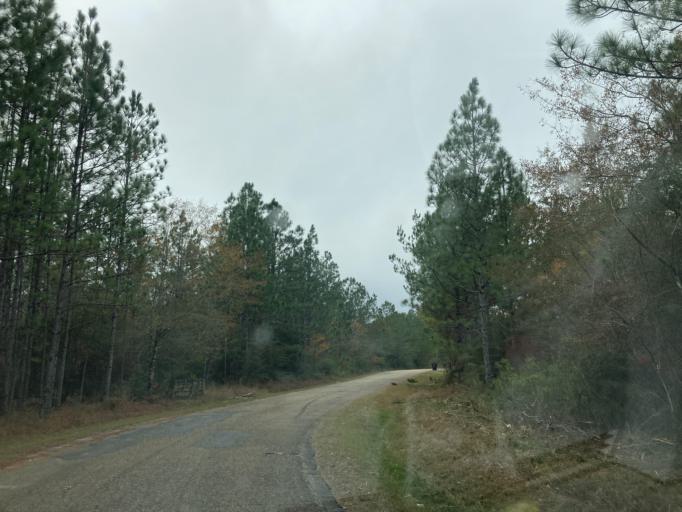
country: US
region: Mississippi
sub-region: Lamar County
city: Lumberton
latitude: 31.0193
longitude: -89.4948
